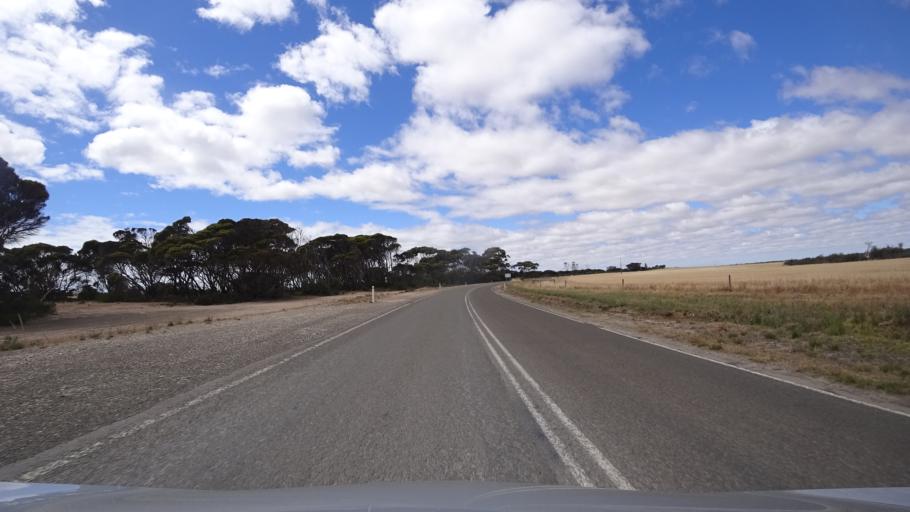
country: AU
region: South Australia
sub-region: Kangaroo Island
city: Kingscote
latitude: -35.6295
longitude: 137.5579
